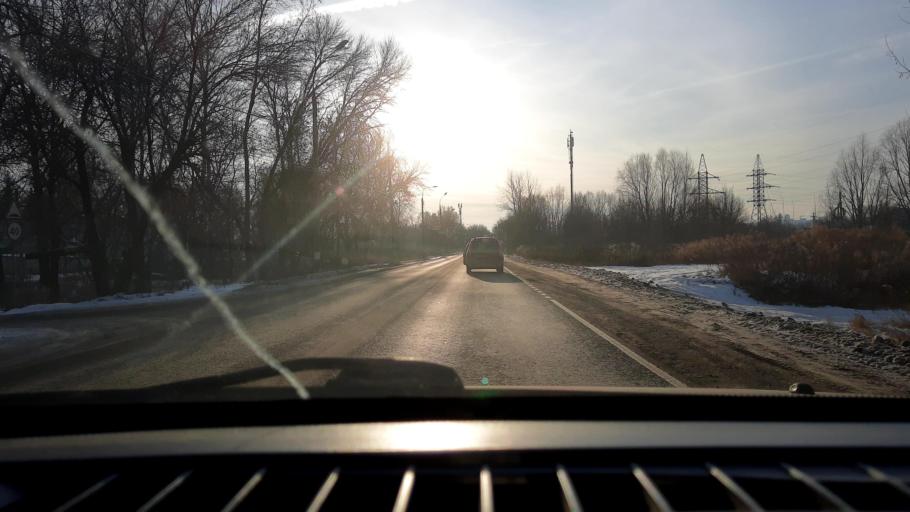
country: RU
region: Nizjnij Novgorod
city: Bor
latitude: 56.3625
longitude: 44.0878
